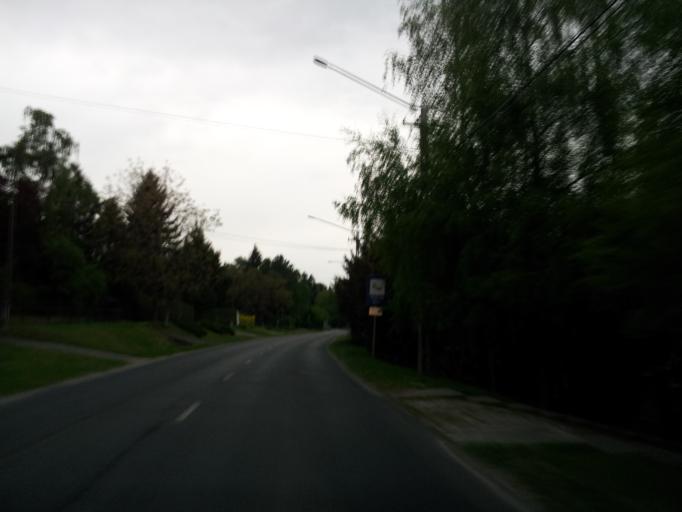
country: HU
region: Pest
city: Dunabogdany
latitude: 47.7994
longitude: 19.0193
